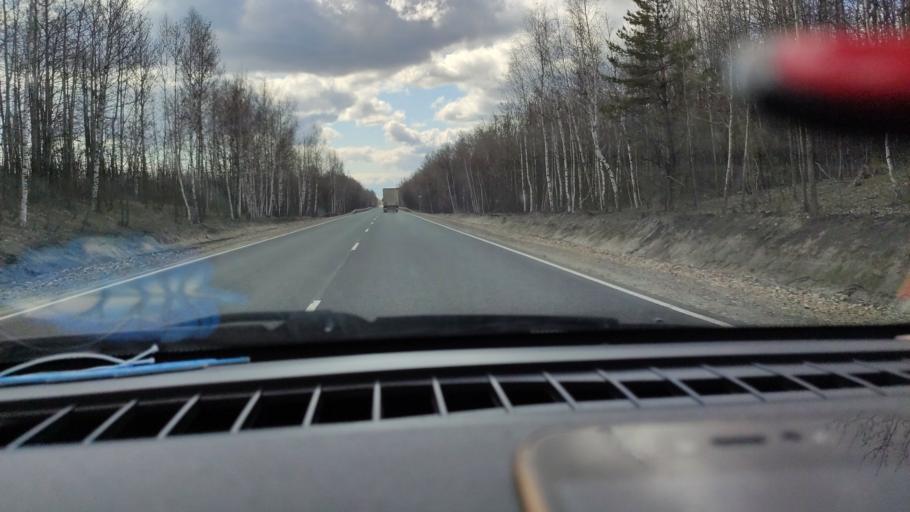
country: RU
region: Saratov
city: Khvalynsk
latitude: 52.4333
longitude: 48.0091
